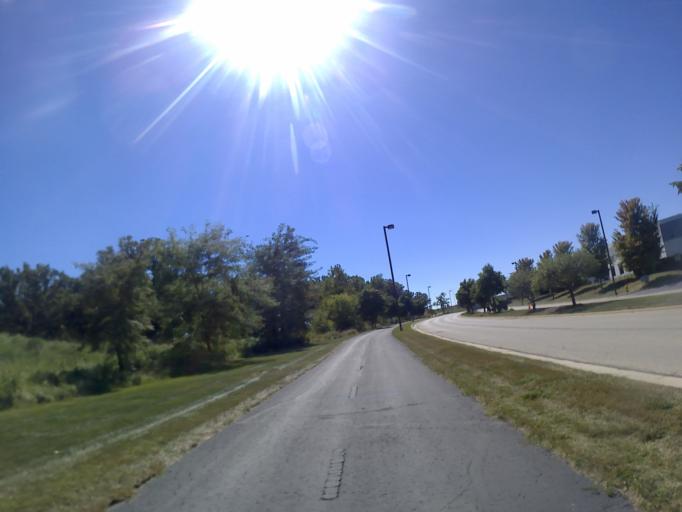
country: US
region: Illinois
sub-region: Cook County
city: Lemont
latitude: 41.6926
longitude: -88.0272
